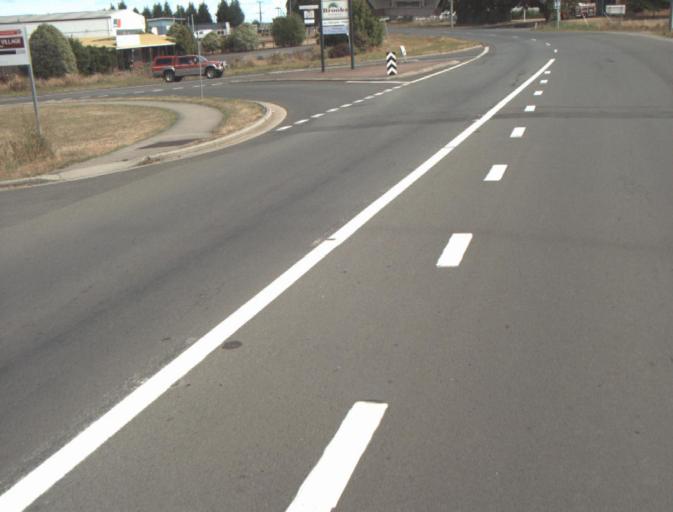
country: AU
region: Tasmania
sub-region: Launceston
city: Mayfield
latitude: -41.3780
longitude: 147.1262
